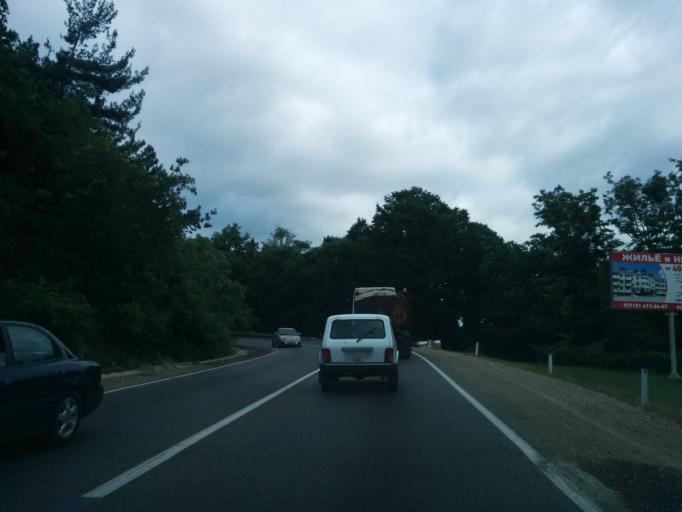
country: RU
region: Krasnodarskiy
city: Agoy
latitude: 44.1282
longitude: 39.0478
